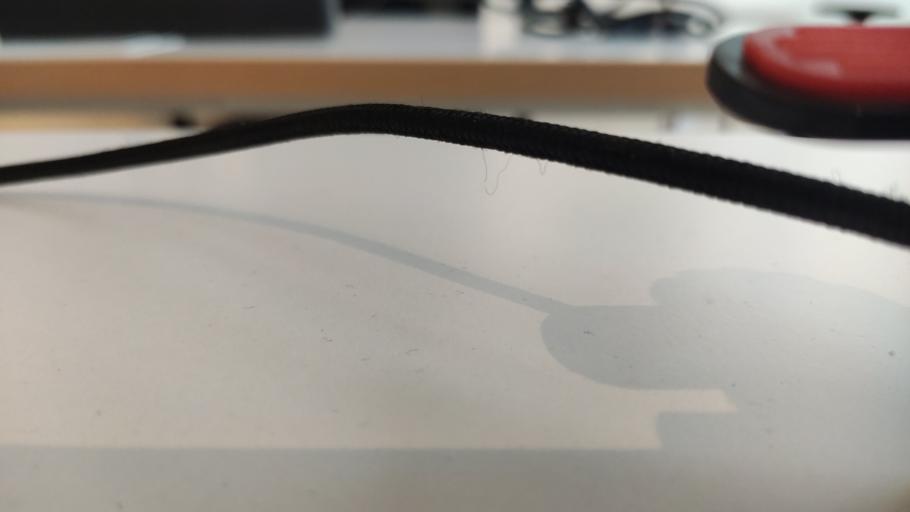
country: RU
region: Moskovskaya
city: Shevlyakovo
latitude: 56.3979
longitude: 36.8631
